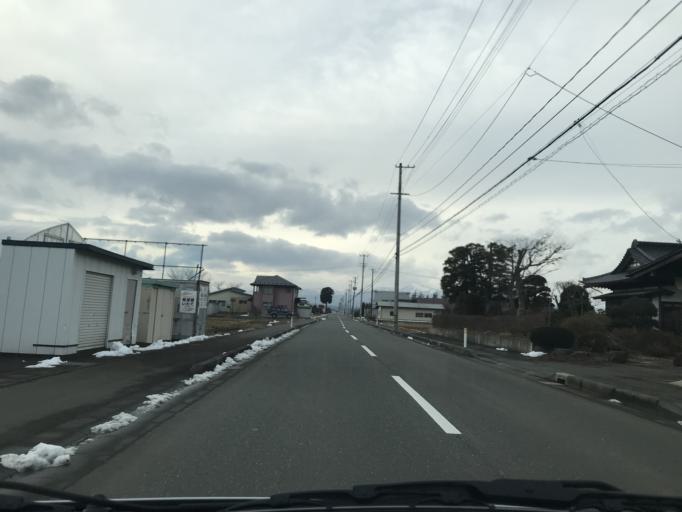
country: JP
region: Iwate
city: Mizusawa
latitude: 39.1545
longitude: 141.1091
